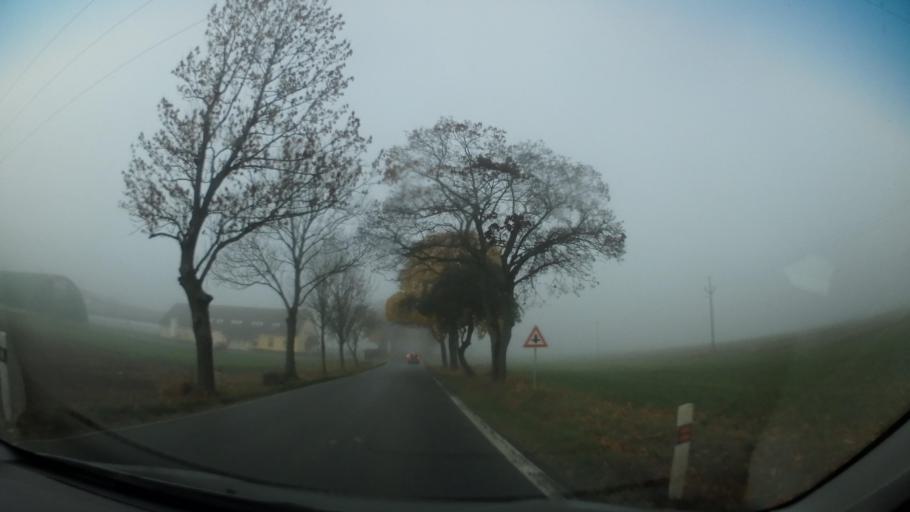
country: CZ
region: Vysocina
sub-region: Okres Zd'ar nad Sazavou
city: Nove Mesto na Morave
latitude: 49.4737
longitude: 16.0694
